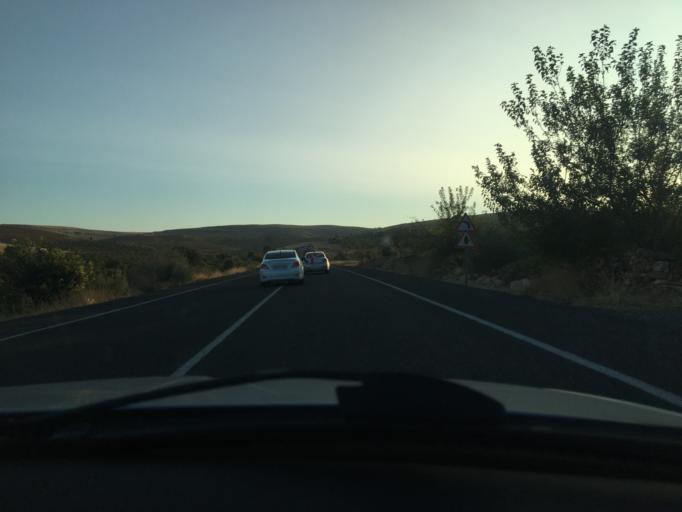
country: TR
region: Sanliurfa
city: Halfeti
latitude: 37.2000
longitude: 37.9679
